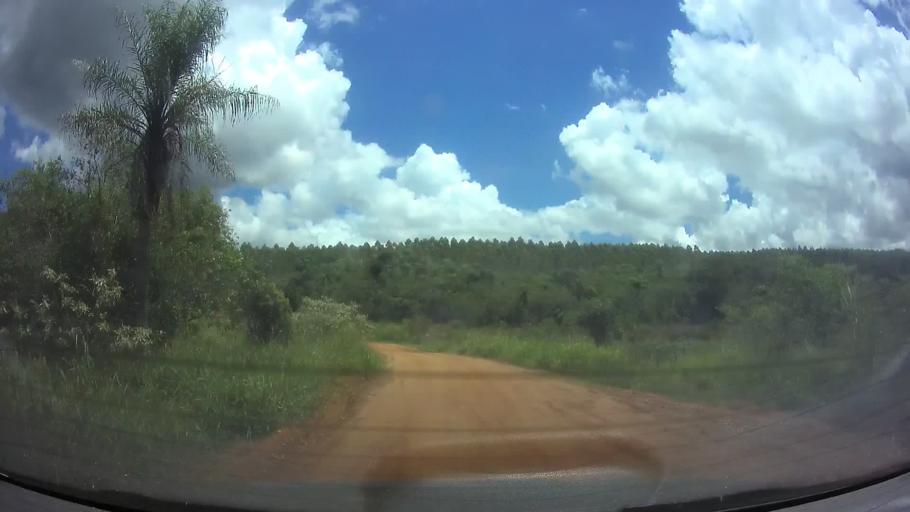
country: PY
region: Paraguari
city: La Colmena
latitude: -25.9641
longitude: -56.7405
